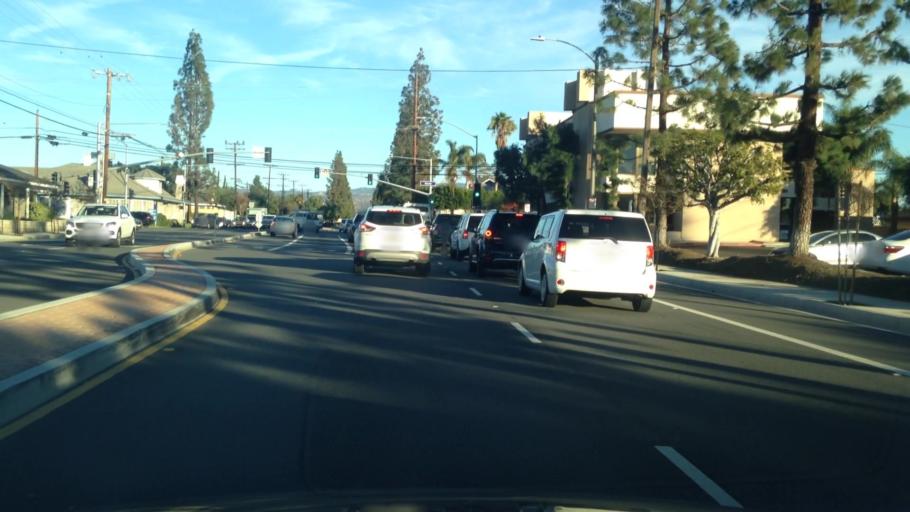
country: US
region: California
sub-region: Orange County
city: Villa Park
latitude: 33.8103
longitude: -117.8231
